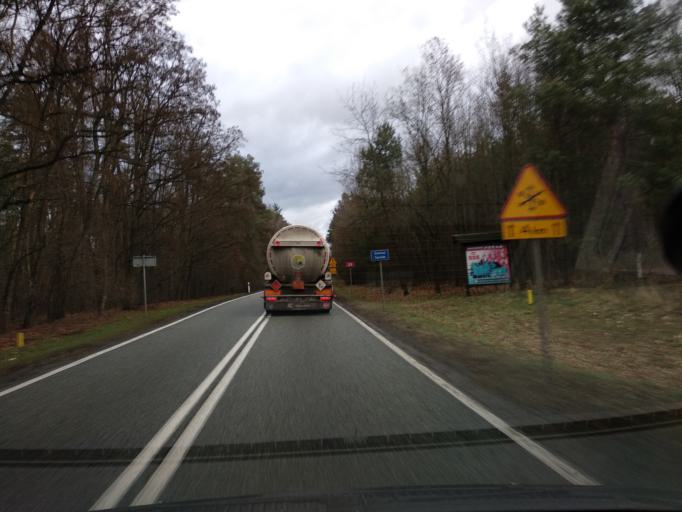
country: PL
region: Lower Silesian Voivodeship
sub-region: Powiat olesnicki
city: Twardogora
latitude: 51.3015
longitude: 17.5366
